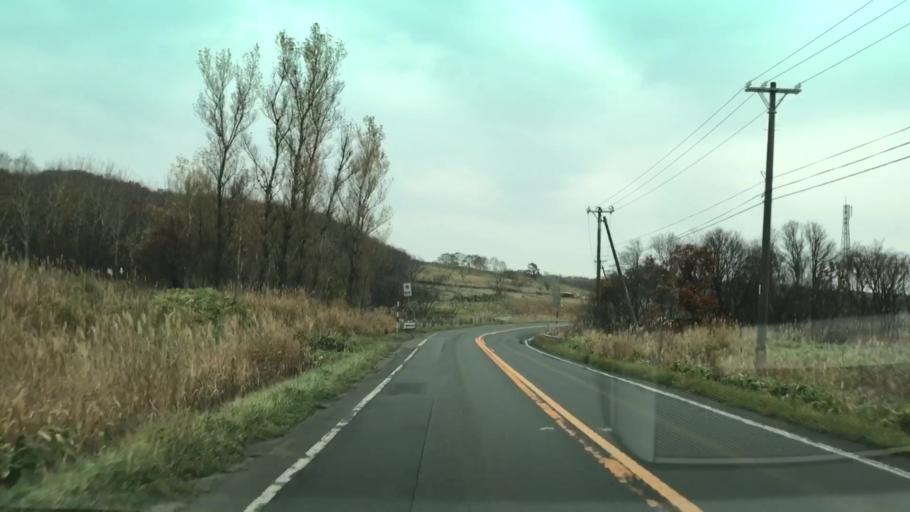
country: JP
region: Hokkaido
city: Ishikari
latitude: 43.3640
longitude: 141.4298
